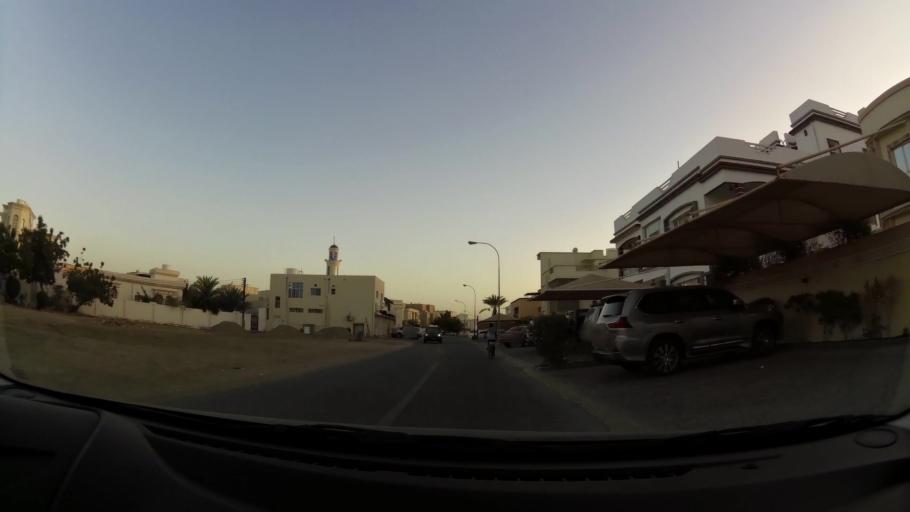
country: OM
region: Muhafazat Masqat
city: As Sib al Jadidah
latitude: 23.5990
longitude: 58.2381
